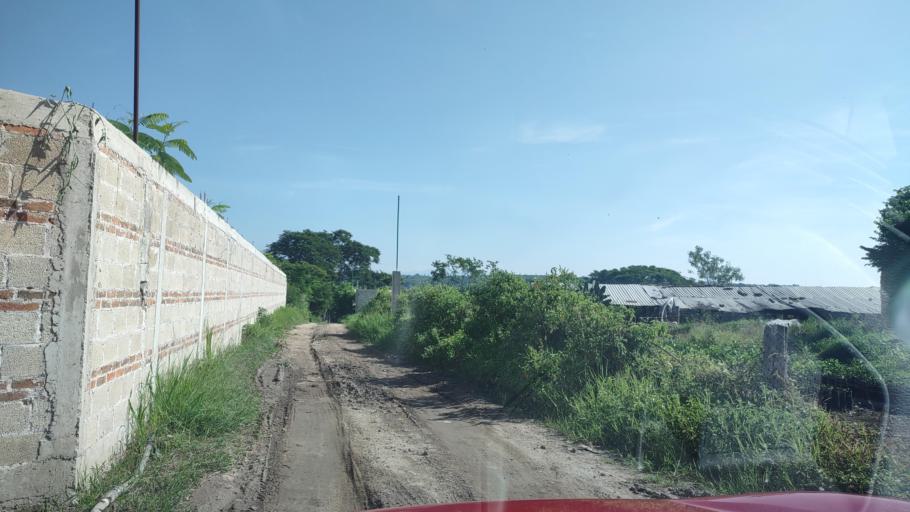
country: MX
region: Veracruz
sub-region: Emiliano Zapata
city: Dos Rios
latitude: 19.4303
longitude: -96.8003
